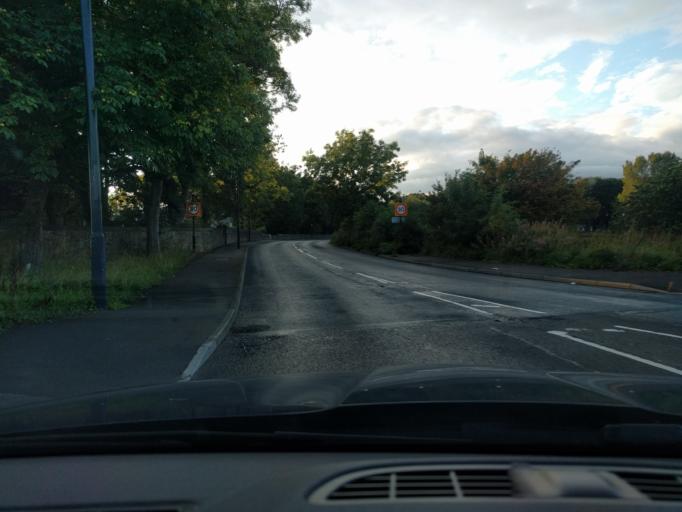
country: GB
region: England
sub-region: Northumberland
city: Backworth
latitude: 55.0373
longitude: -1.5245
